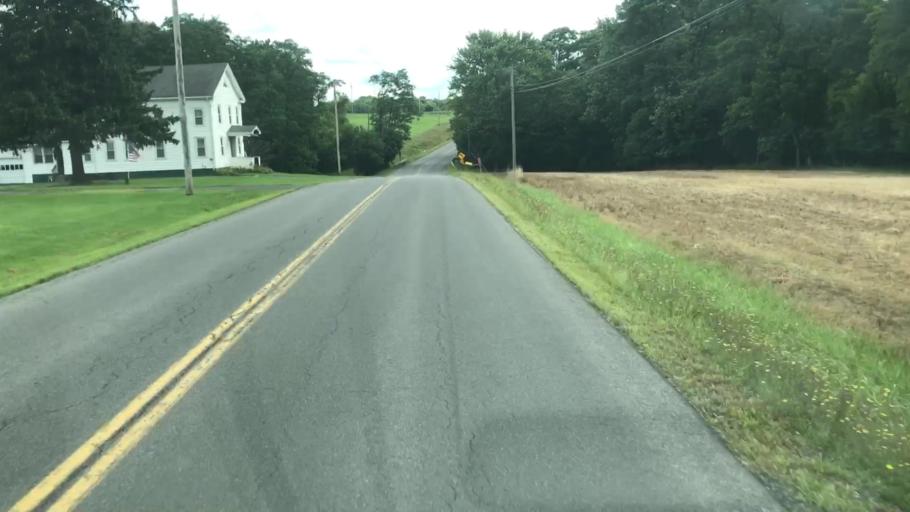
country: US
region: New York
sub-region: Cayuga County
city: Melrose Park
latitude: 42.9186
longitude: -76.5232
